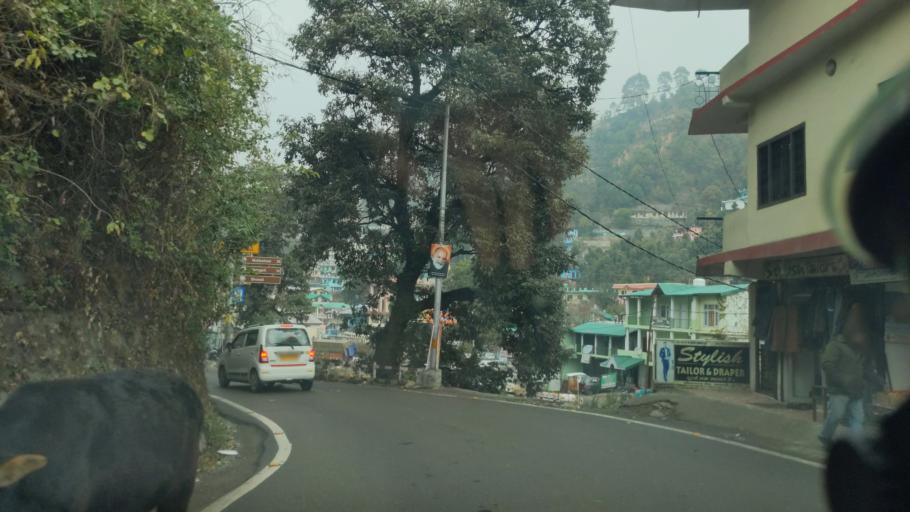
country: IN
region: Uttarakhand
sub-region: Naini Tal
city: Bhowali
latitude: 29.3823
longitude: 79.5212
